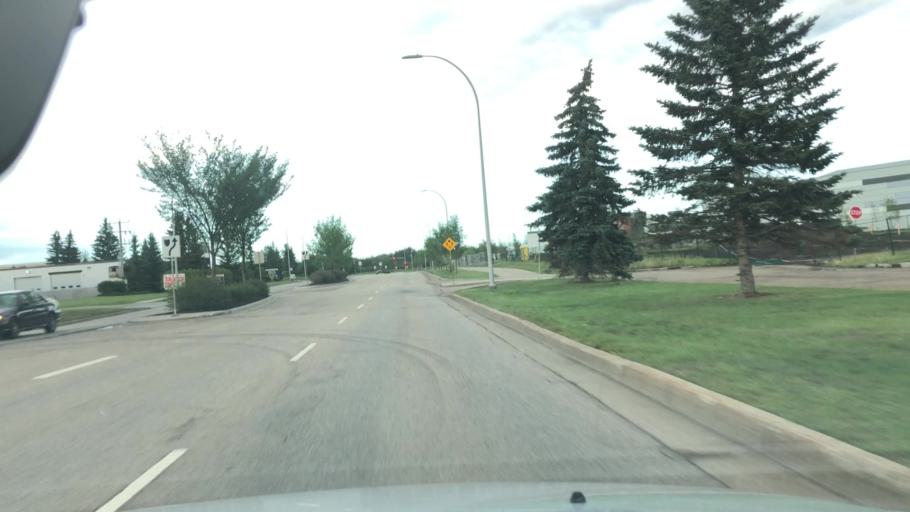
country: CA
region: Alberta
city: St. Albert
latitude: 53.6314
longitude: -113.5912
